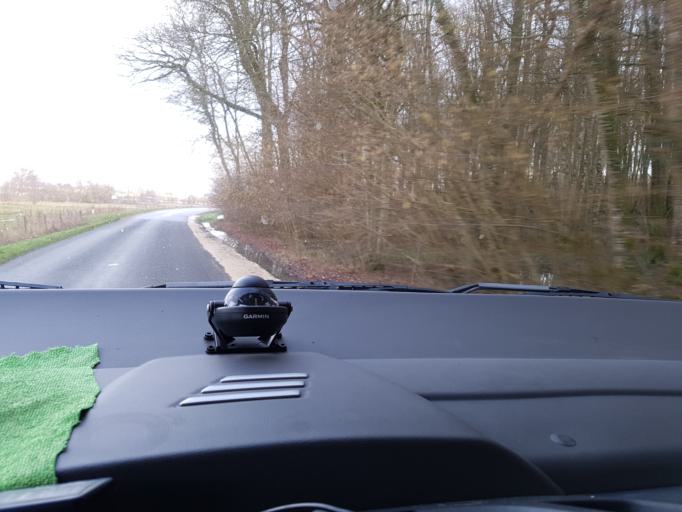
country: FR
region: Champagne-Ardenne
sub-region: Departement des Ardennes
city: Tournes
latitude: 49.7612
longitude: 4.6361
